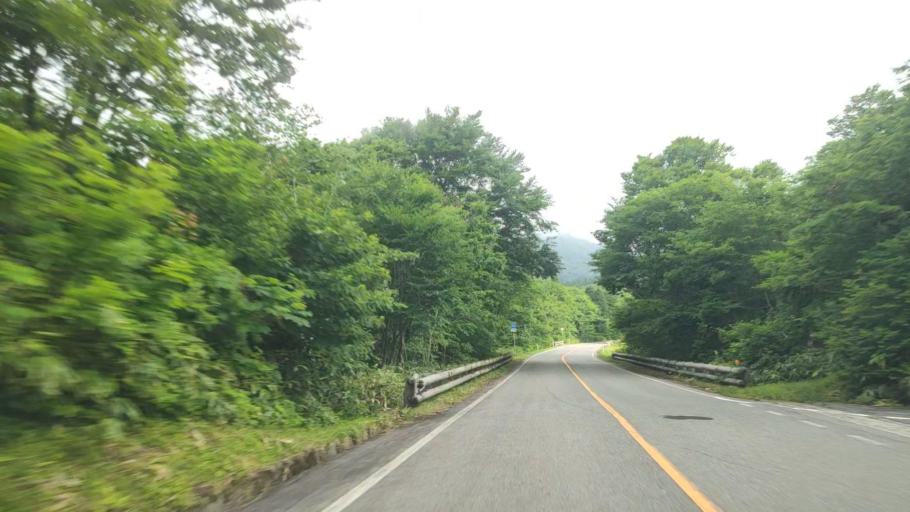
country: JP
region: Tottori
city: Kurayoshi
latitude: 35.3435
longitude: 133.5890
